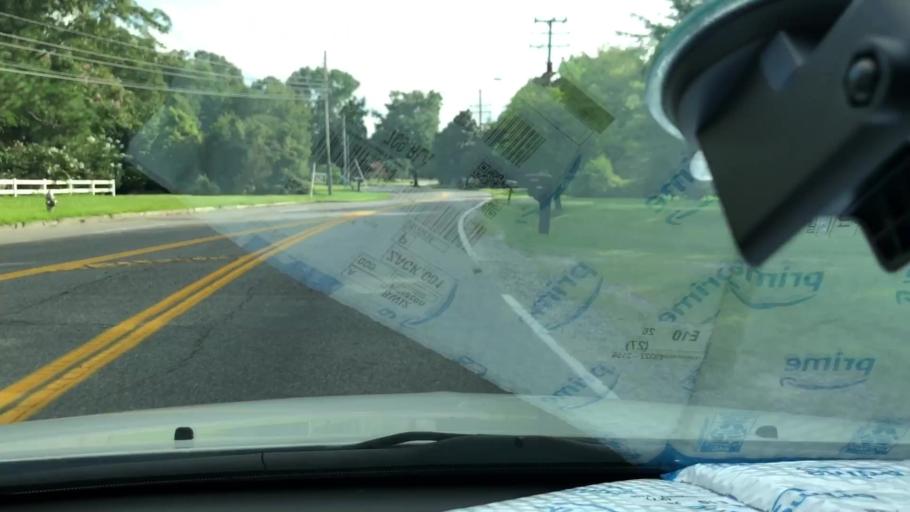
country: US
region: Virginia
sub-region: City of Chesapeake
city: Chesapeake
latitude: 36.7093
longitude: -76.2721
